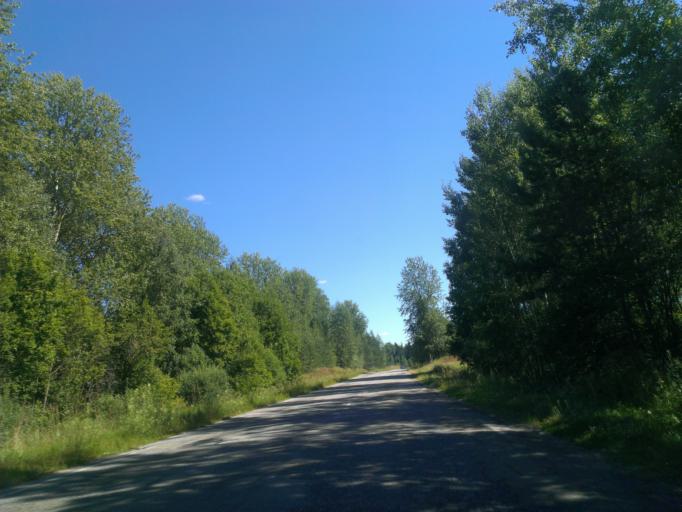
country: LV
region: Incukalns
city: Incukalns
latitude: 57.0294
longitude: 24.7336
